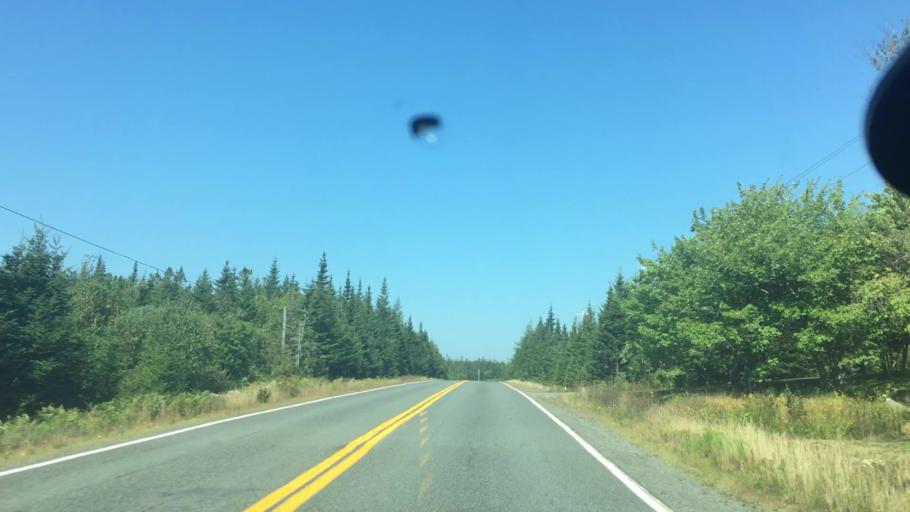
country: CA
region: Nova Scotia
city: Antigonish
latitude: 45.0043
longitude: -62.1027
